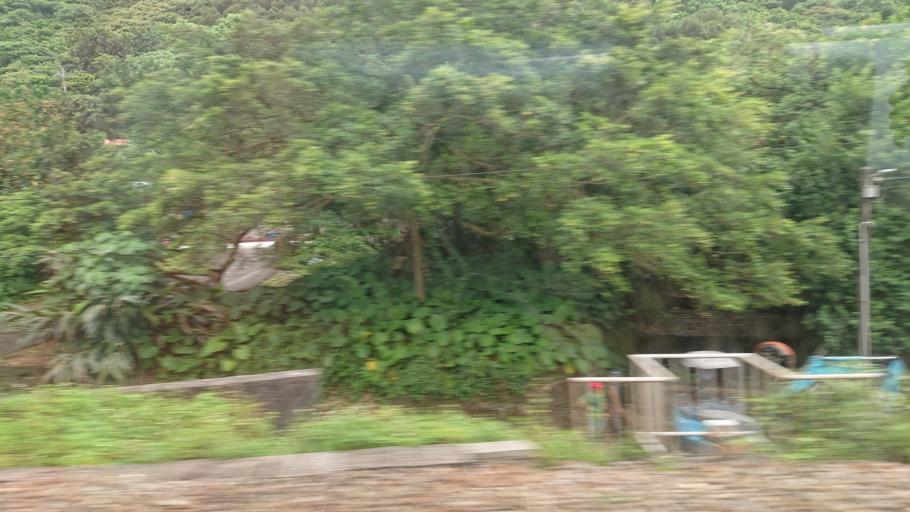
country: TW
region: Taiwan
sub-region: Keelung
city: Keelung
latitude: 24.9743
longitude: 121.9370
